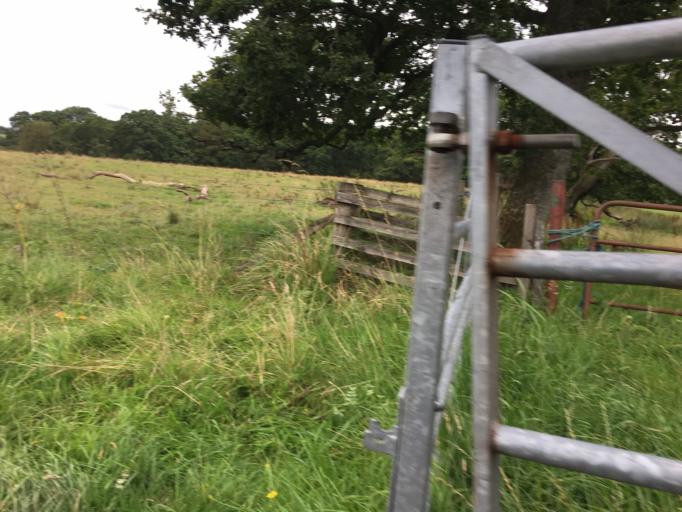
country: GB
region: Scotland
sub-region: Stirling
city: Killearn
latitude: 56.0430
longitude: -4.3964
